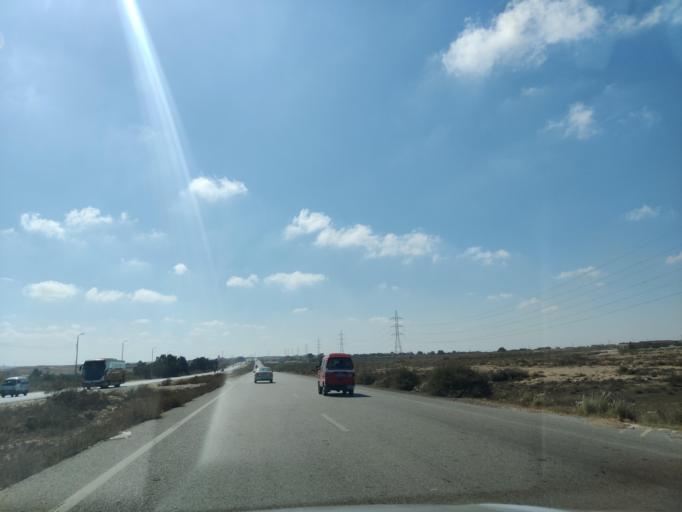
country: EG
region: Muhafazat Matruh
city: Al `Alamayn
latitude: 31.0472
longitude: 28.3378
